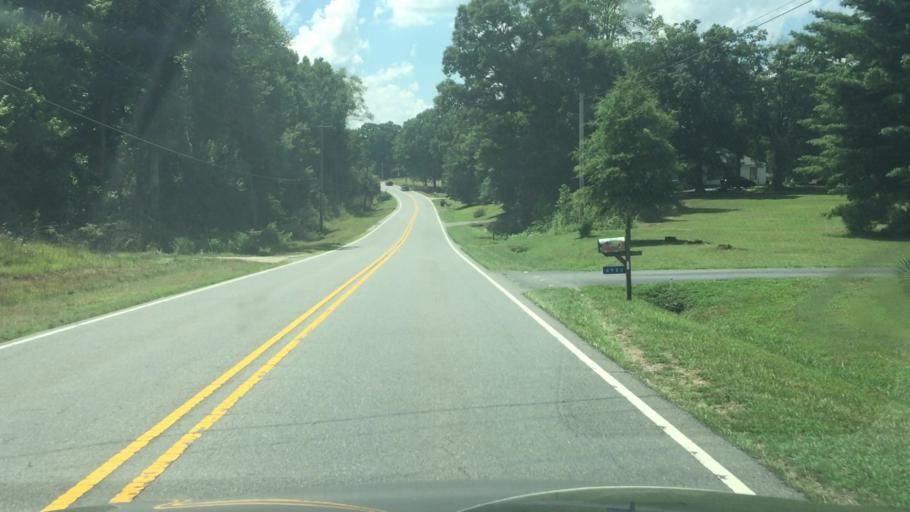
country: US
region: North Carolina
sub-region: Rowan County
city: Enochville
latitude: 35.5750
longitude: -80.6675
